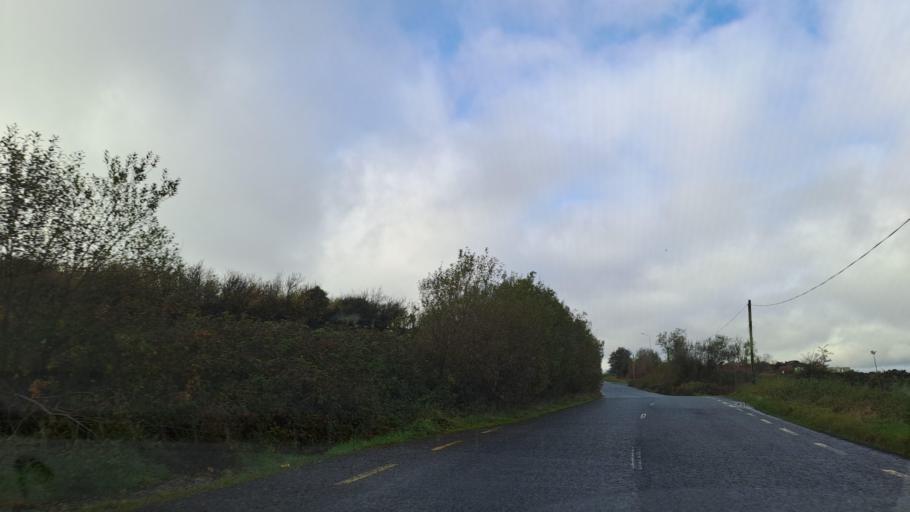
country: IE
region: Ulster
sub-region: An Cabhan
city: Bailieborough
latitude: 53.8910
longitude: -7.0200
